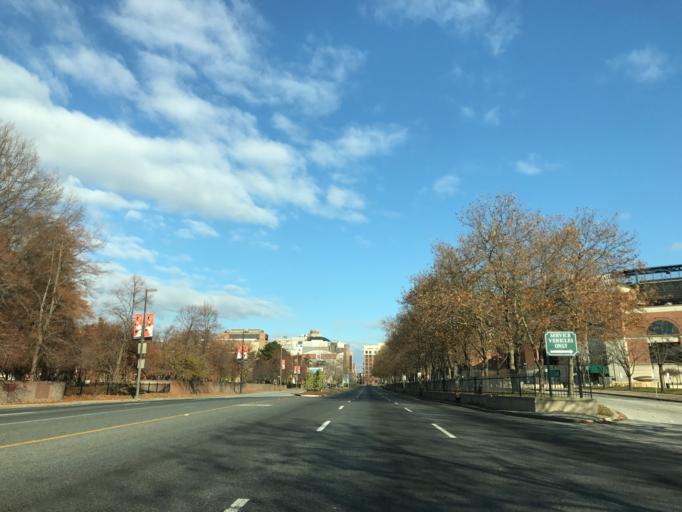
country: US
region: Maryland
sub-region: City of Baltimore
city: Baltimore
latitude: 39.2815
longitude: -76.6232
